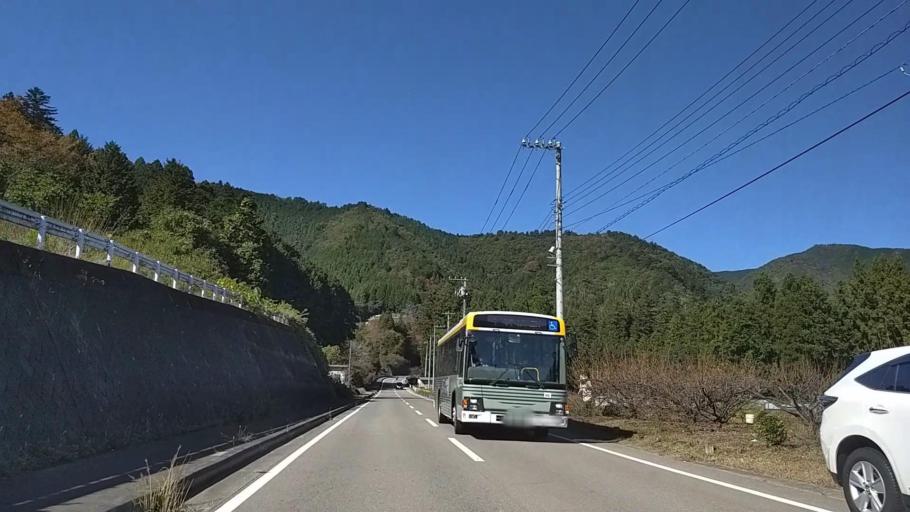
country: JP
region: Yamanashi
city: Uenohara
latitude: 35.6622
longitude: 139.0891
